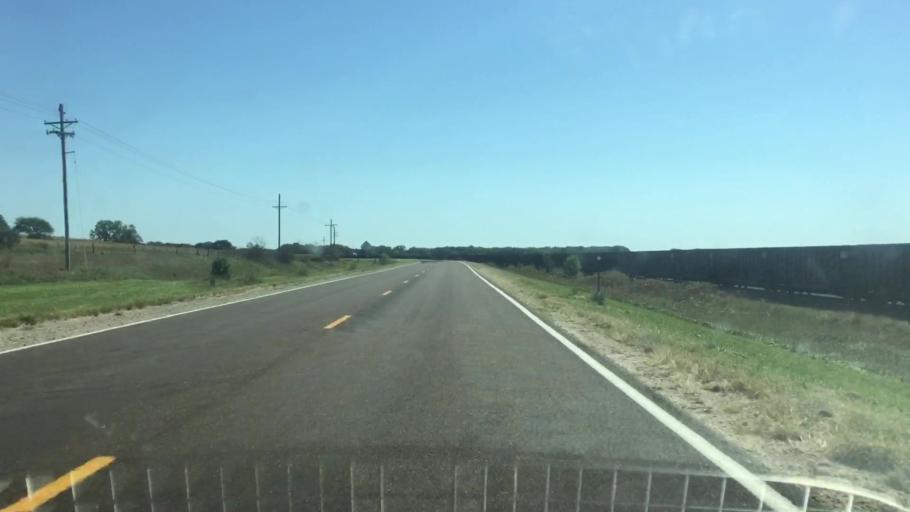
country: US
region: Nebraska
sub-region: Jefferson County
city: Fairbury
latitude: 40.0883
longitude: -97.1204
